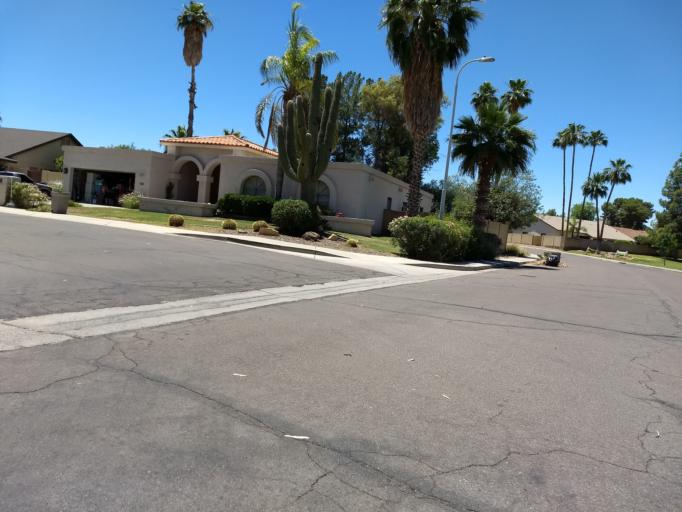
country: US
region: Arizona
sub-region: Maricopa County
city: San Carlos
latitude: 33.3292
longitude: -111.9073
